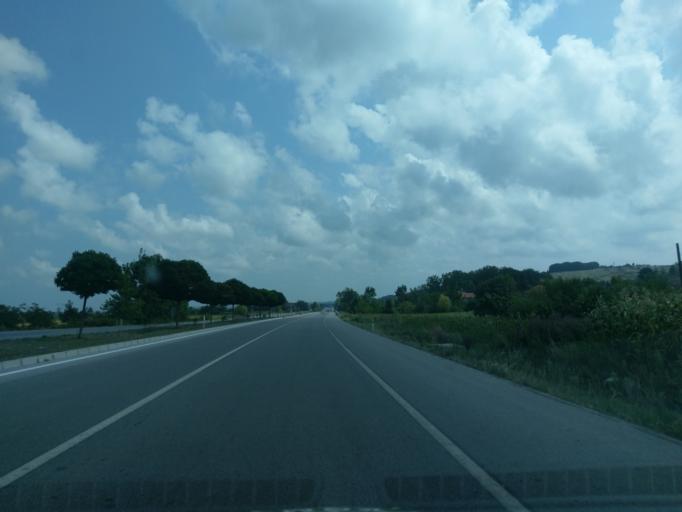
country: TR
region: Samsun
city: Alacam
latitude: 41.6117
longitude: 35.7133
